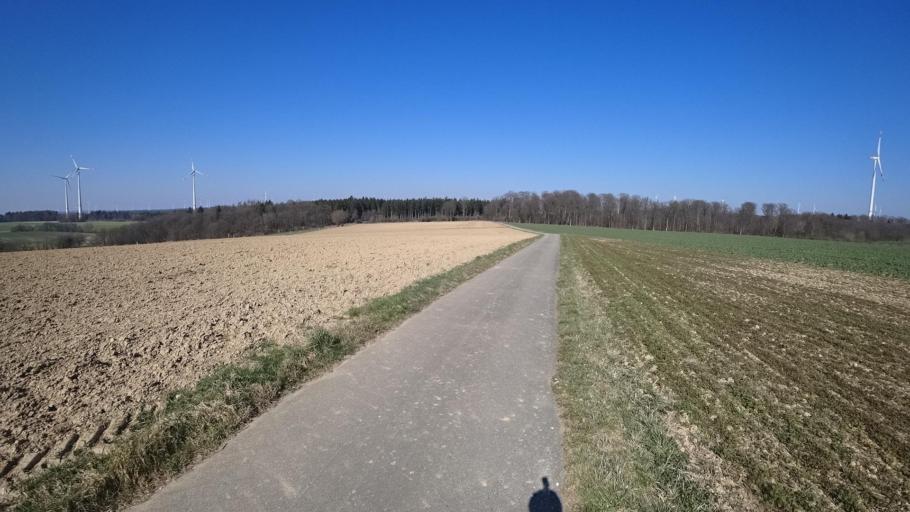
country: DE
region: Rheinland-Pfalz
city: Wahlbach
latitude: 50.0034
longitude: 7.5932
